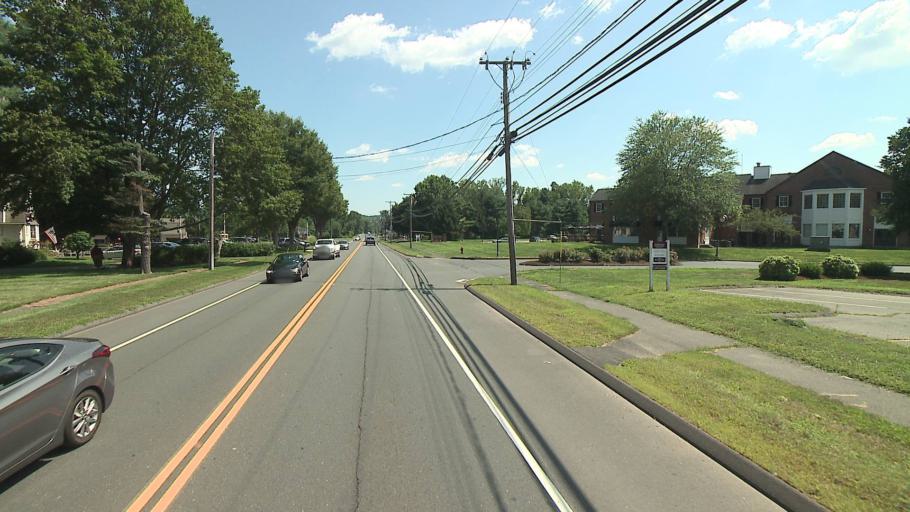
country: US
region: Connecticut
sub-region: Hartford County
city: Farmington
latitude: 41.7354
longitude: -72.8388
